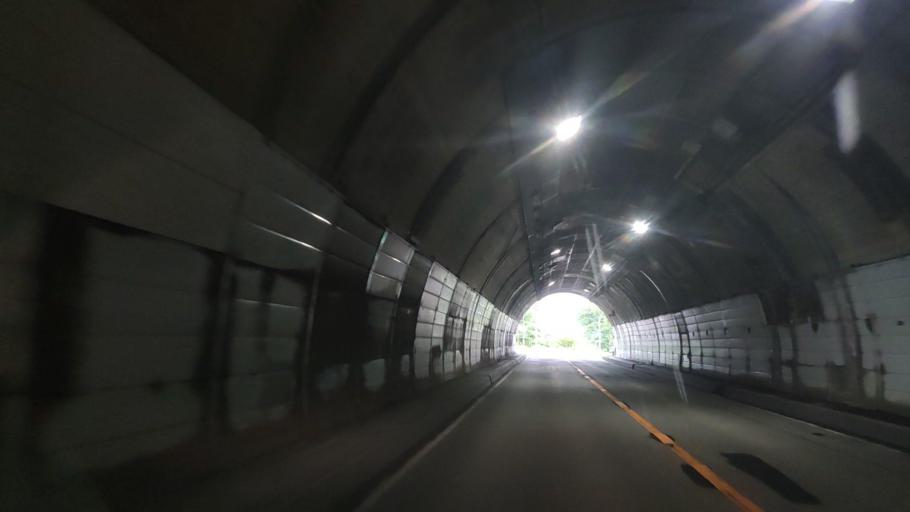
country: JP
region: Hokkaido
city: Niseko Town
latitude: 42.5942
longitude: 140.5995
